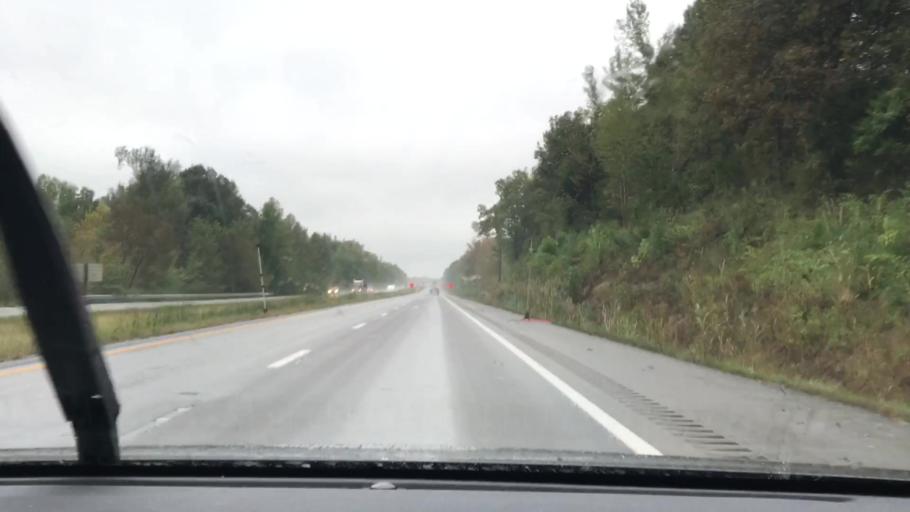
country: US
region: Kentucky
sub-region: Hopkins County
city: Nortonville
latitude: 37.1644
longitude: -87.4554
